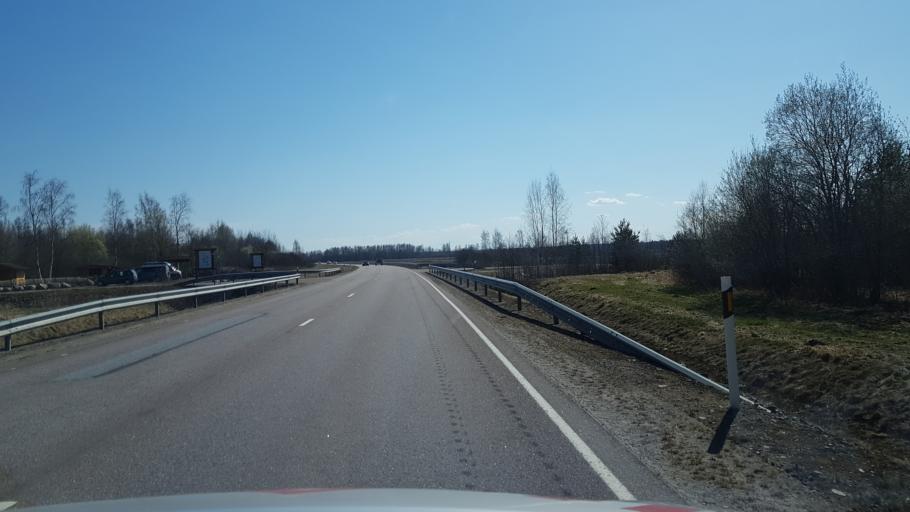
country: EE
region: Jogevamaa
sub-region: Mustvee linn
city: Mustvee
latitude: 58.8208
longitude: 26.9364
